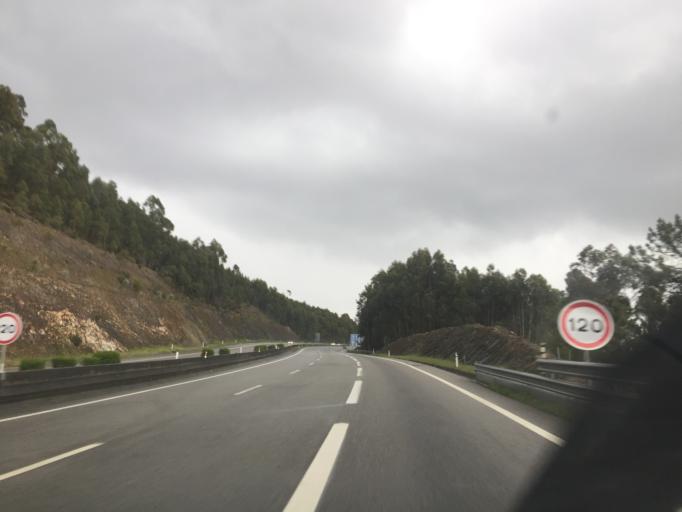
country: PT
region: Aveiro
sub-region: Agueda
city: Valongo
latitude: 40.6569
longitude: -8.3834
